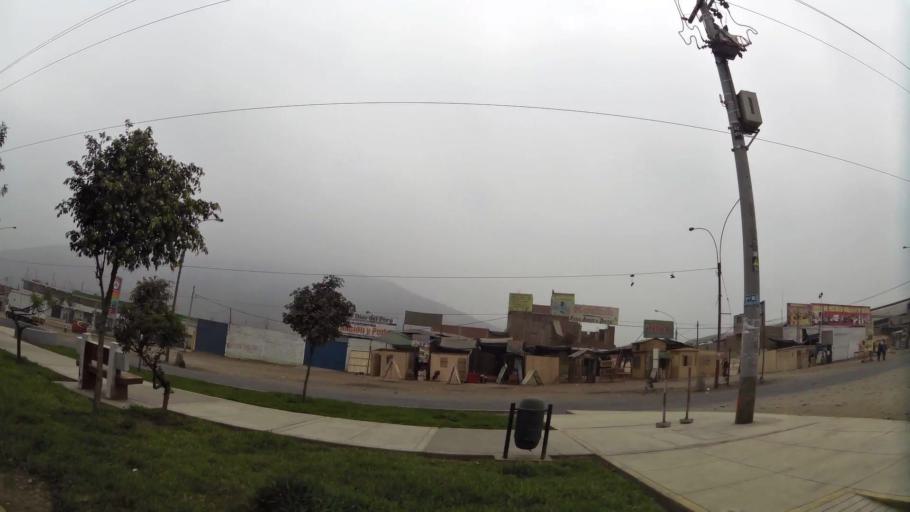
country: PE
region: Lima
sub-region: Lima
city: Urb. Santo Domingo
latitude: -11.9240
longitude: -76.9625
